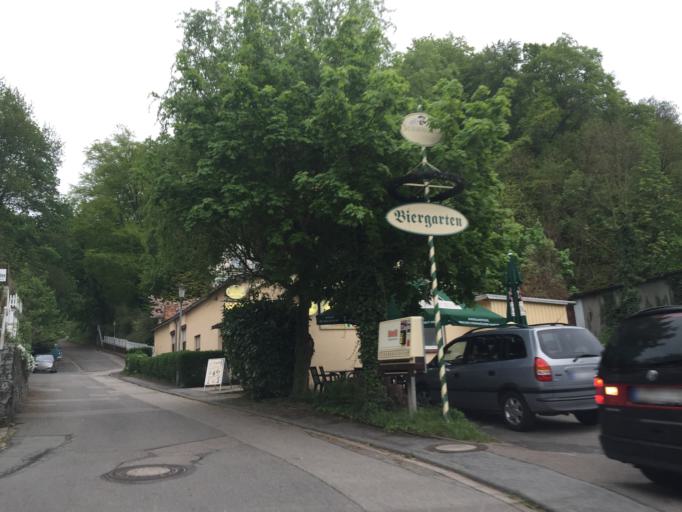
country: DE
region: Baden-Wuerttemberg
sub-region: Karlsruhe Region
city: Weinheim
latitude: 49.5279
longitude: 8.6741
